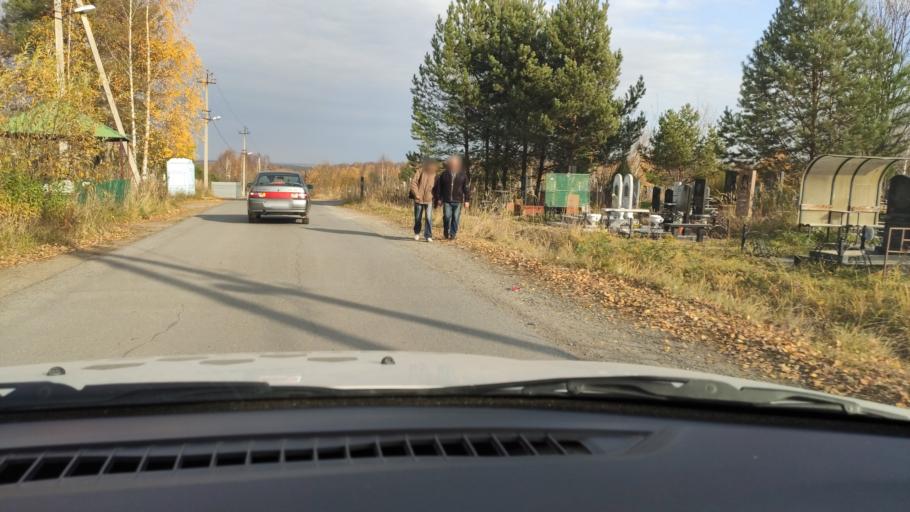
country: RU
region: Perm
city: Kondratovo
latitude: 58.0652
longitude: 56.1440
